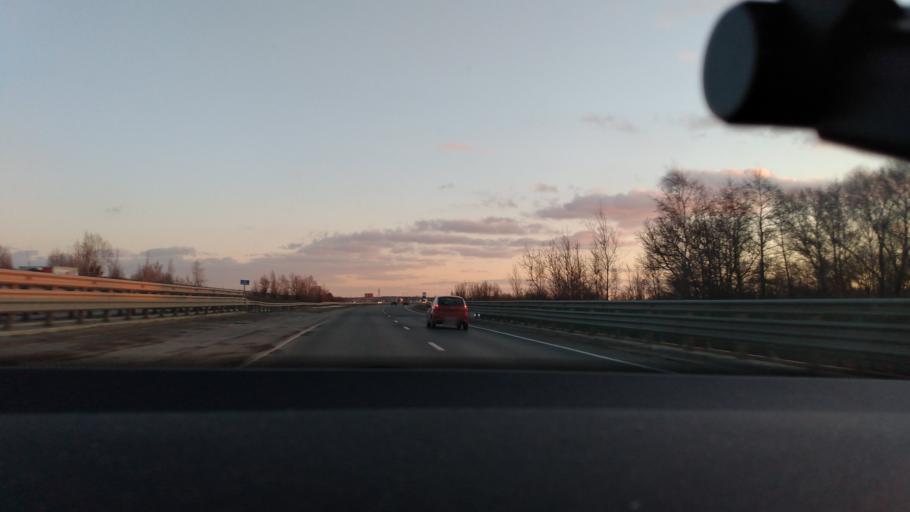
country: RU
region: Moskovskaya
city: Kolomna
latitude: 55.0992
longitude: 38.9010
